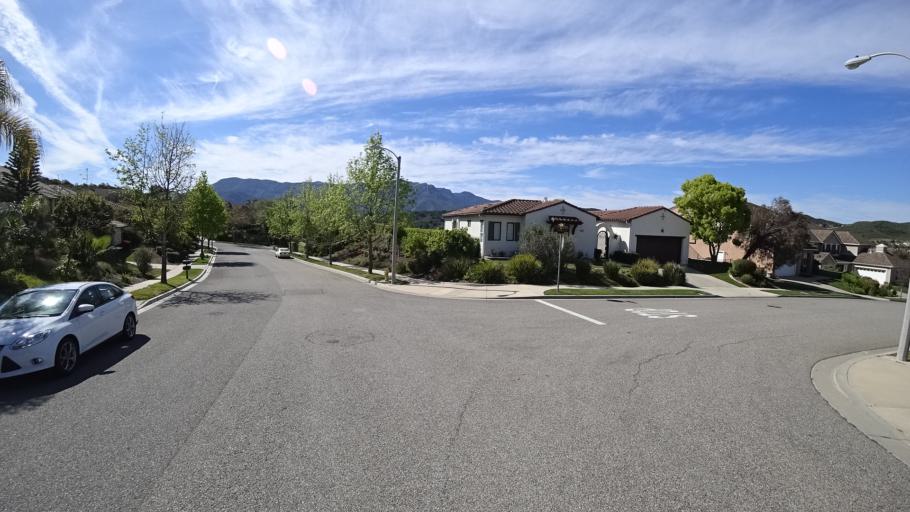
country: US
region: California
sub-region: Ventura County
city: Casa Conejo
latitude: 34.1750
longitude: -118.9654
